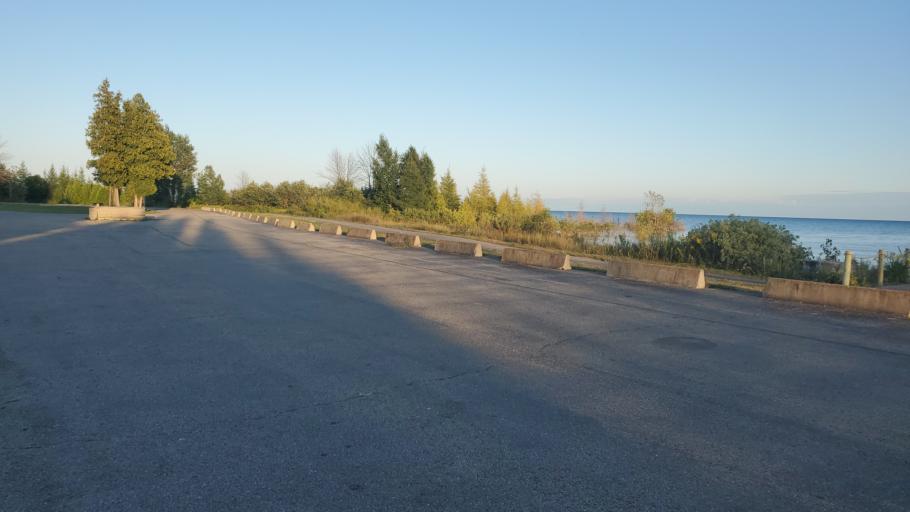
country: US
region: Michigan
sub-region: Schoolcraft County
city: Manistique
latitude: 45.9464
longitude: -86.2354
